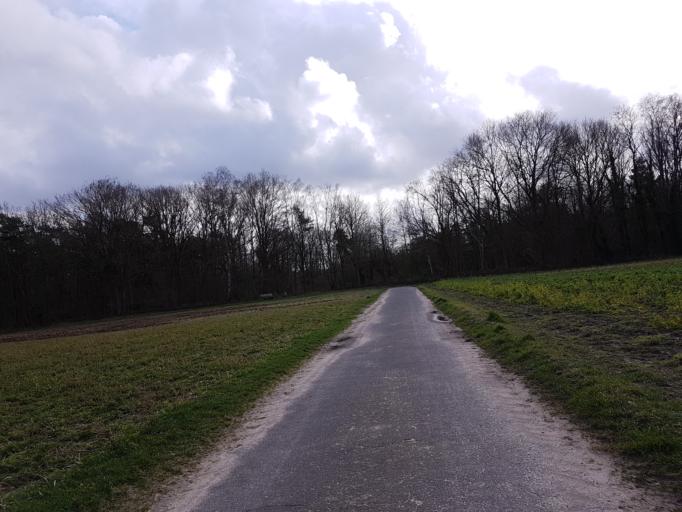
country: DE
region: North Rhine-Westphalia
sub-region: Regierungsbezirk Dusseldorf
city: Bruggen
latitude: 51.2521
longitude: 6.1932
